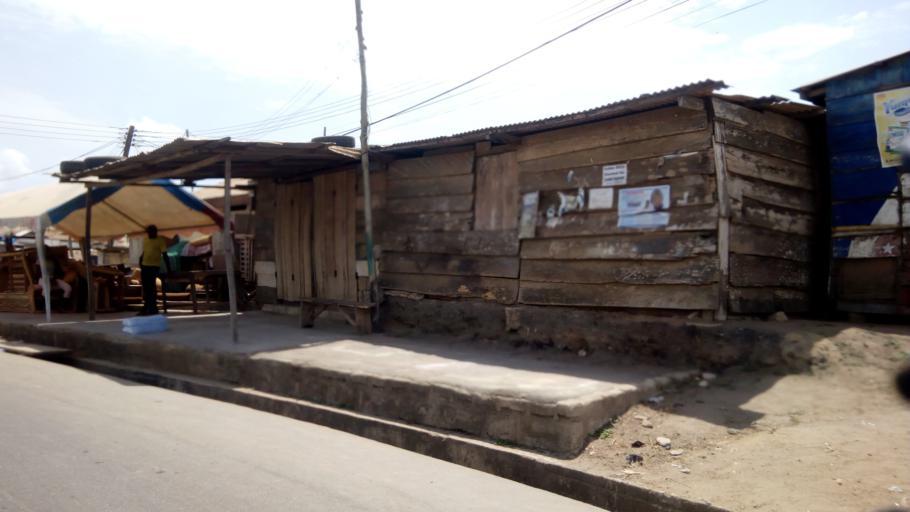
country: GH
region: Central
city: Cape Coast
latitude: 5.1264
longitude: -1.2731
